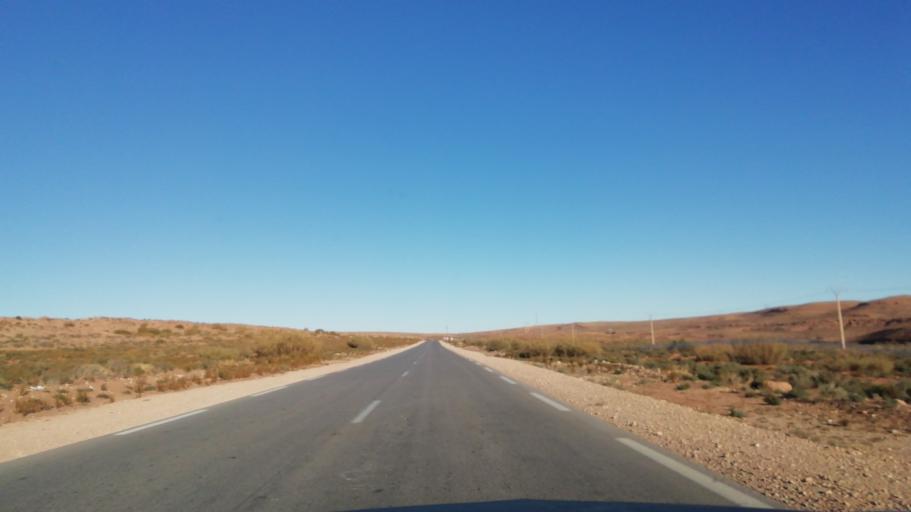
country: DZ
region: El Bayadh
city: El Abiodh Sidi Cheikh
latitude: 33.1671
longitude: 0.4205
